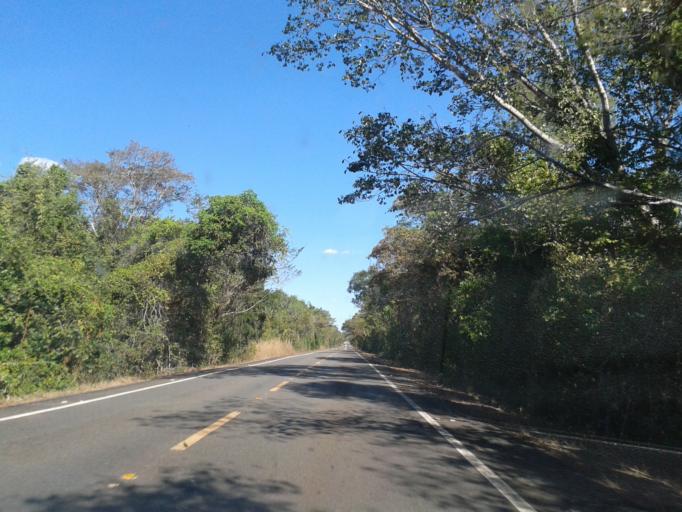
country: BR
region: Goias
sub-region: Sao Miguel Do Araguaia
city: Sao Miguel do Araguaia
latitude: -13.8175
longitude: -50.3424
